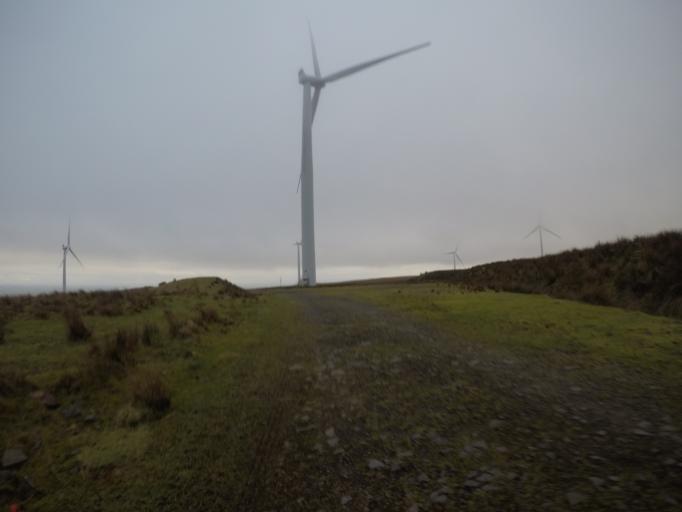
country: GB
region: Scotland
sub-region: North Ayrshire
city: Dalry
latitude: 55.7372
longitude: -4.7771
